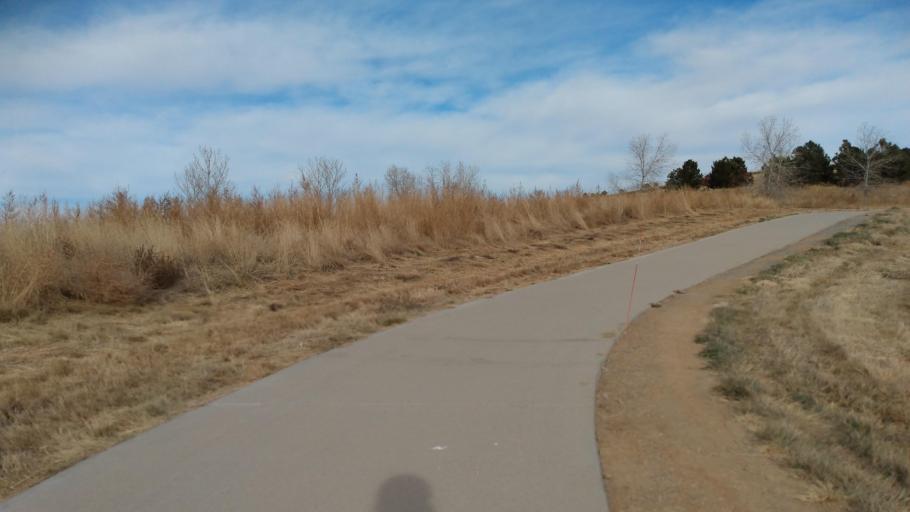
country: US
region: Colorado
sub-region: Boulder County
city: Lafayette
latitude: 39.9968
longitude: -105.0524
